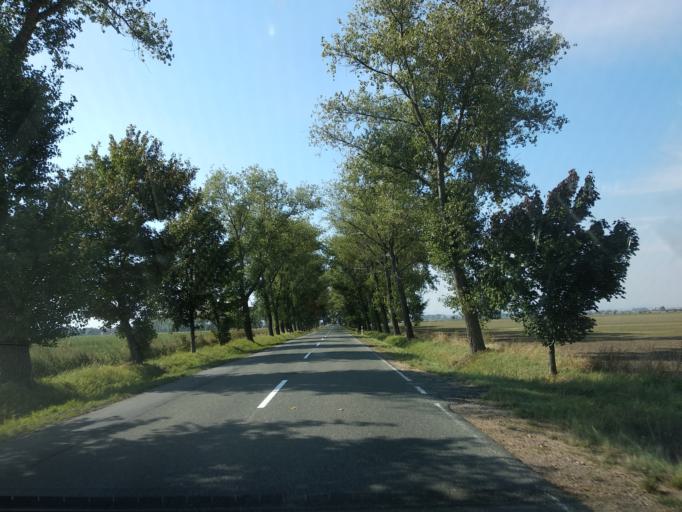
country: PL
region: Lower Silesian Voivodeship
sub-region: Powiat strzelinski
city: Strzelin
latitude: 50.8581
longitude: 17.0636
